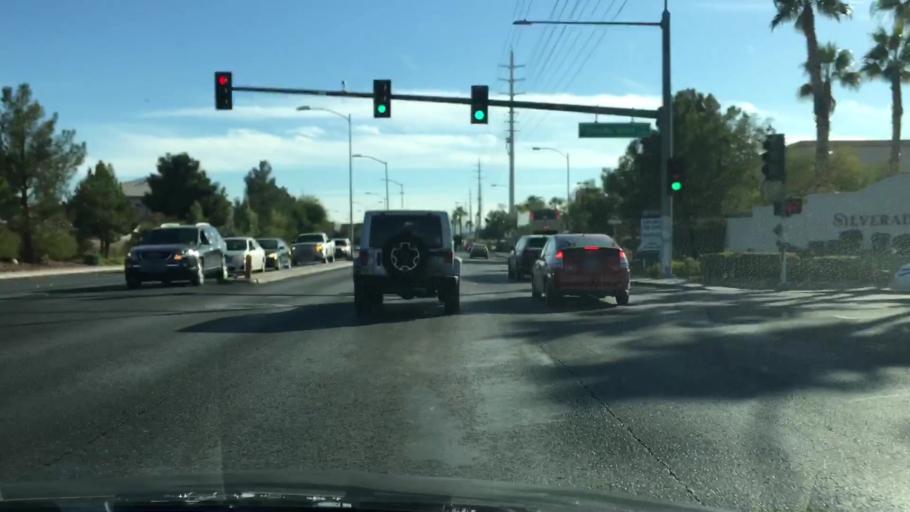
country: US
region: Nevada
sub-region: Clark County
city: Whitney
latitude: 36.0133
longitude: -115.1189
